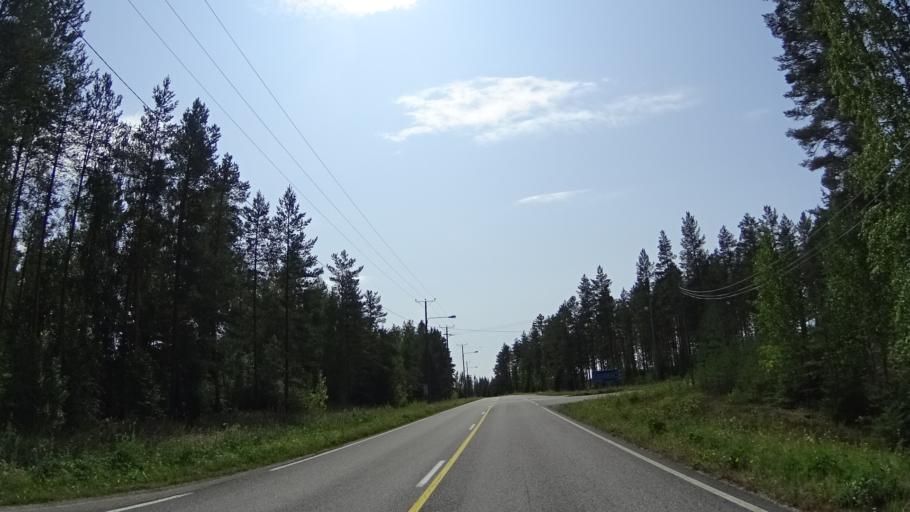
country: FI
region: Pirkanmaa
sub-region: Ylae-Pirkanmaa
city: Maenttae
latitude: 61.8835
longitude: 24.7912
